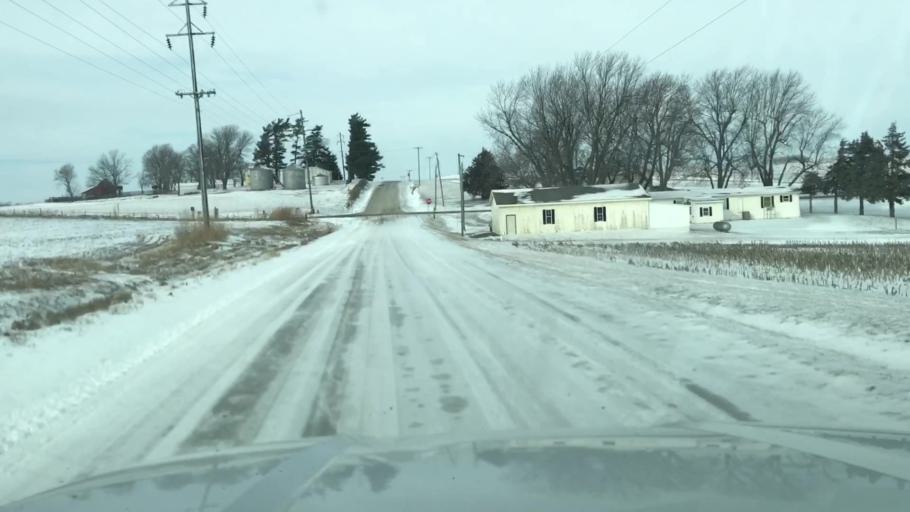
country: US
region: Missouri
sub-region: Holt County
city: Mound City
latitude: 40.1301
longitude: -95.0875
